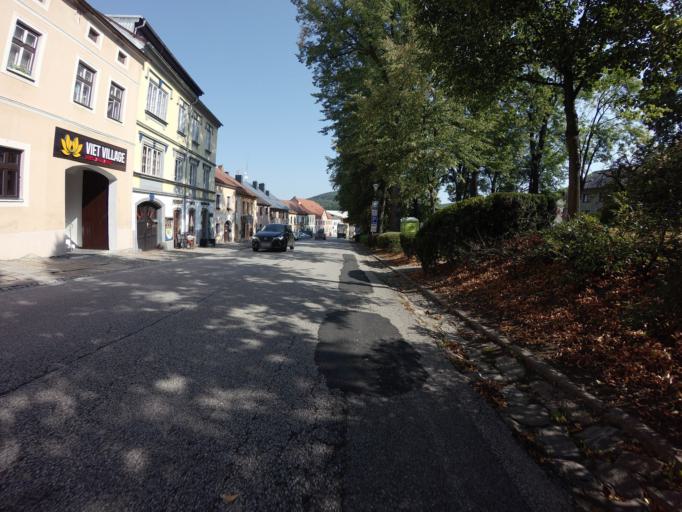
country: CZ
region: Jihocesky
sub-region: Okres Cesky Krumlov
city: Vyssi Brod
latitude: 48.6150
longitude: 14.3117
